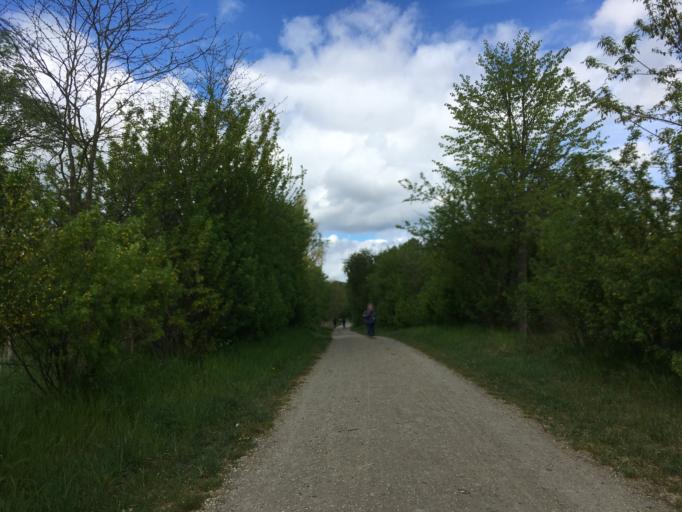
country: DE
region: Berlin
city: Blankenfelde
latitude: 52.6219
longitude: 13.3946
